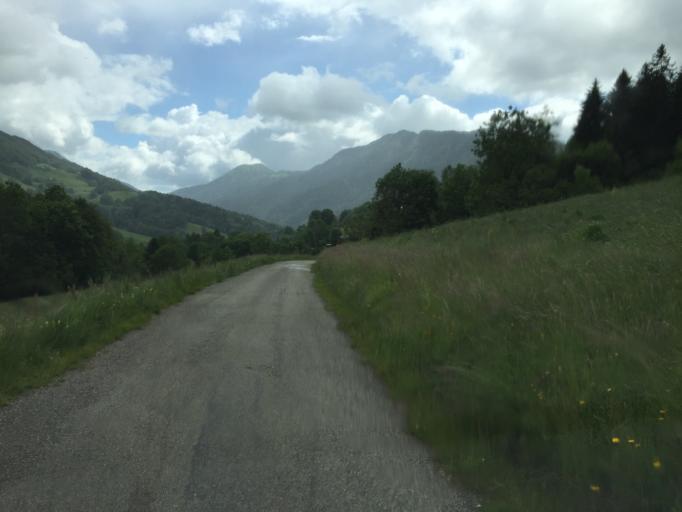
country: FR
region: Rhone-Alpes
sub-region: Departement de la Savoie
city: Cruet
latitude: 45.6178
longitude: 6.1144
